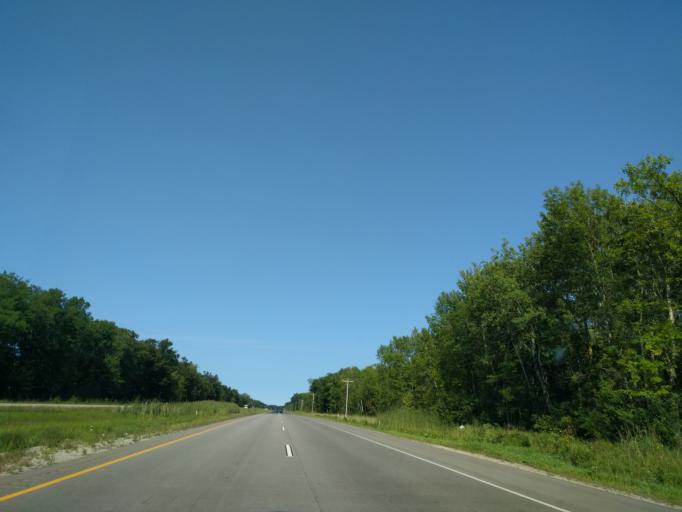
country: US
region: Wisconsin
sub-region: Oconto County
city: Oconto
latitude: 44.8368
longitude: -87.9169
